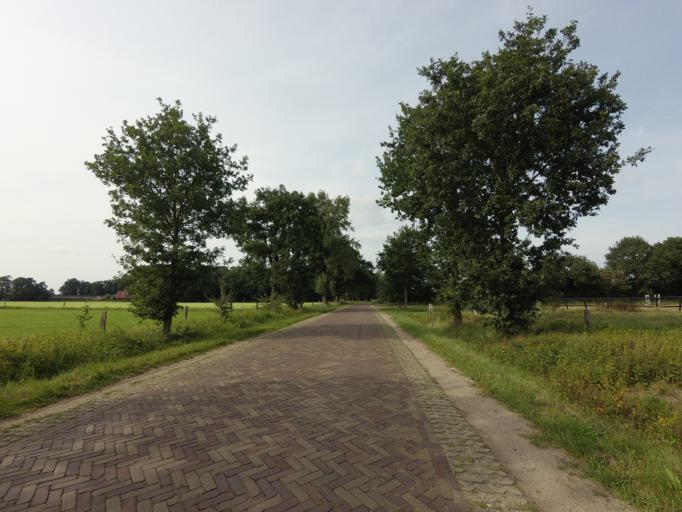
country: DE
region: Lower Saxony
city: Getelo
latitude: 52.4390
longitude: 6.8301
